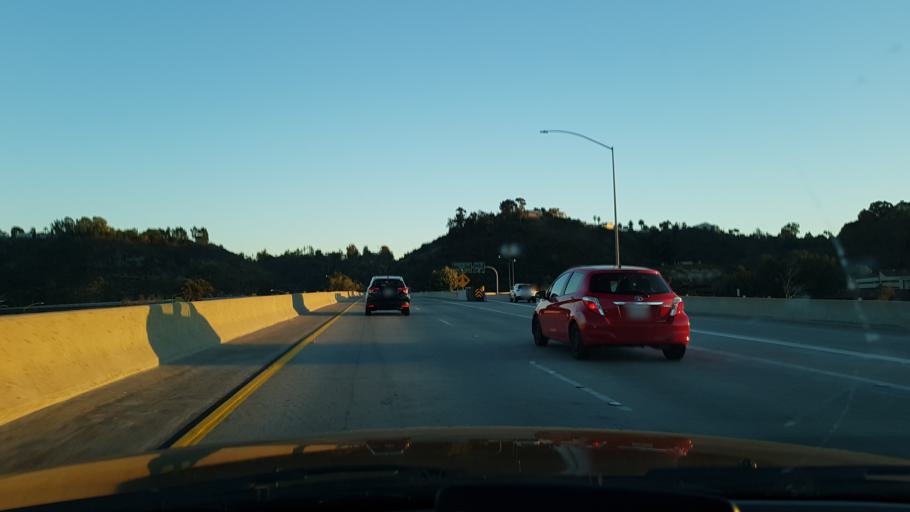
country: US
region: California
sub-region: San Diego County
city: San Diego
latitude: 32.7823
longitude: -117.1140
